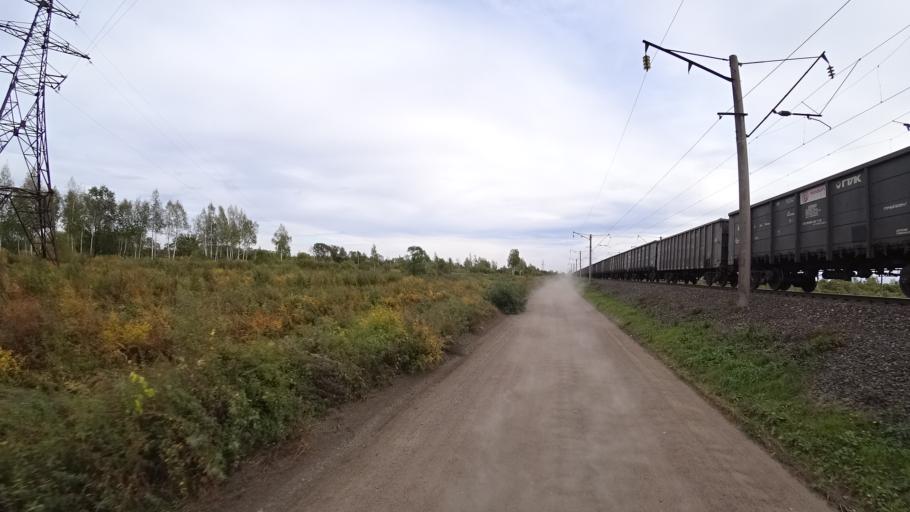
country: RU
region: Amur
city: Arkhara
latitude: 49.3689
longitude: 130.1420
